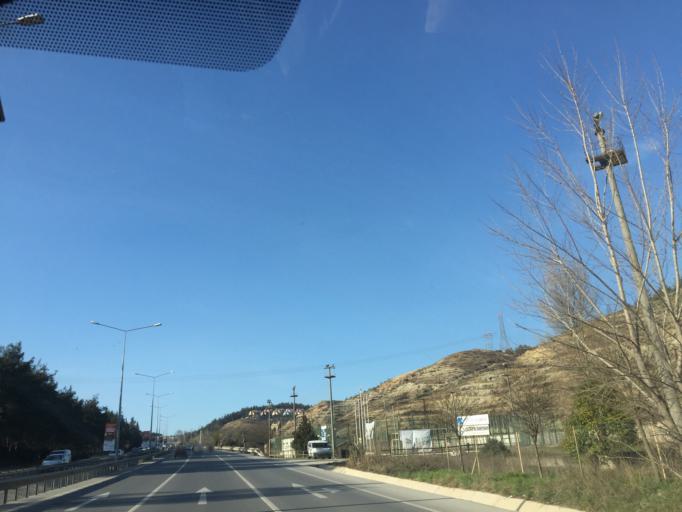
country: TR
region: Bursa
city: Niluefer
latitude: 40.3065
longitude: 28.9380
